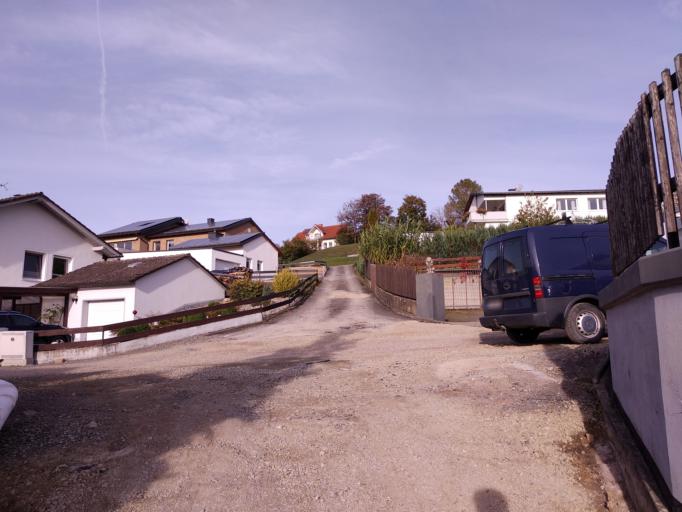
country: DE
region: North Rhine-Westphalia
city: Beverungen
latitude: 51.6744
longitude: 9.3694
